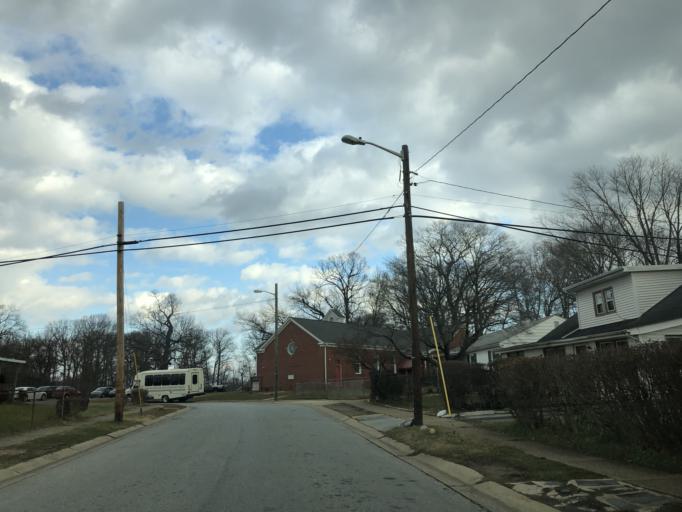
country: US
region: Delaware
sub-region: New Castle County
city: Wilmington Manor
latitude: 39.7046
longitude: -75.5536
